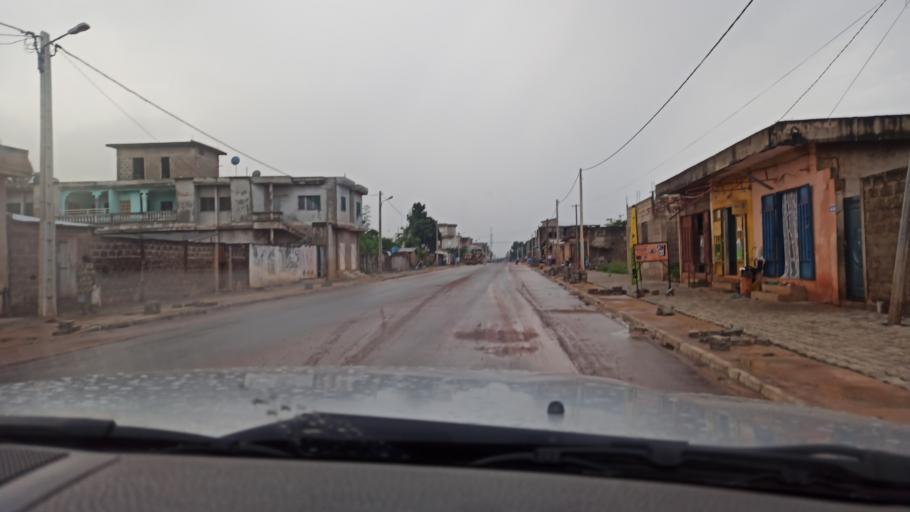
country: BJ
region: Queme
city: Porto-Novo
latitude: 6.4936
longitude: 2.6461
